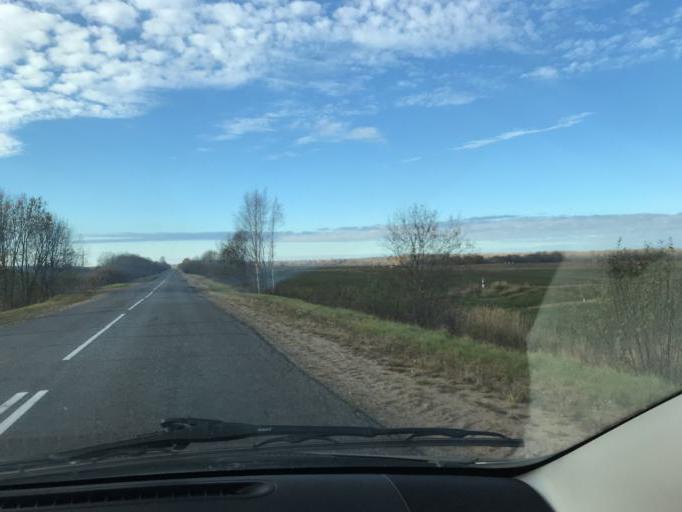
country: BY
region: Vitebsk
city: Haradok
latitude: 55.4104
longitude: 29.7537
